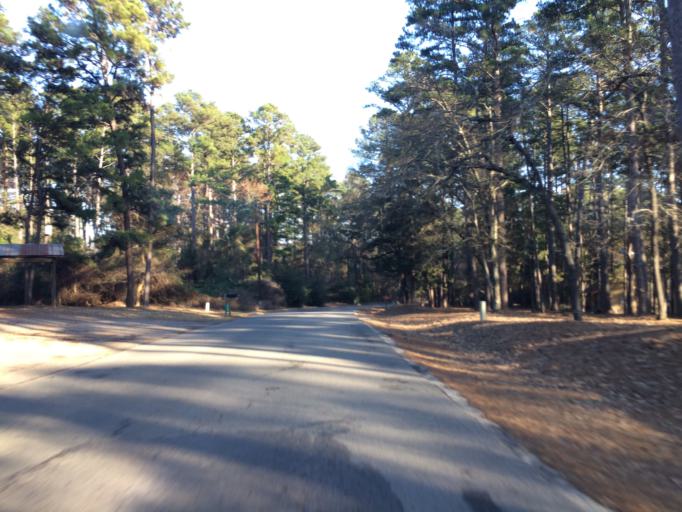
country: US
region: Texas
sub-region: Wood County
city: Hawkins
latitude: 32.7111
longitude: -95.1912
